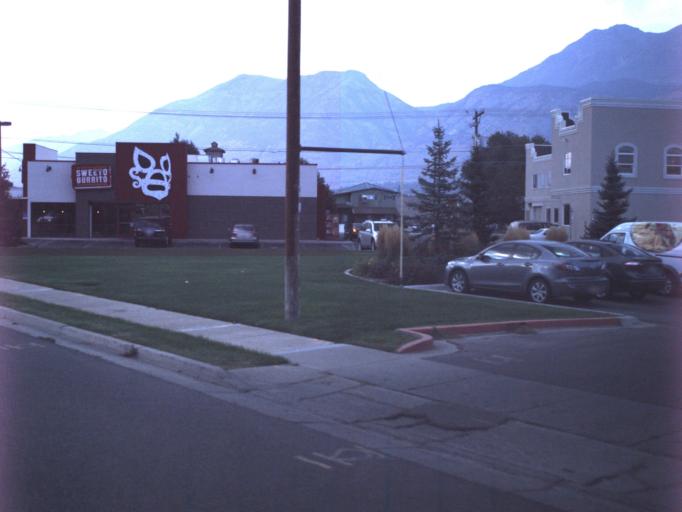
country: US
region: Utah
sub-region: Utah County
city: Lindon
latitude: 40.3329
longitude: -111.7127
